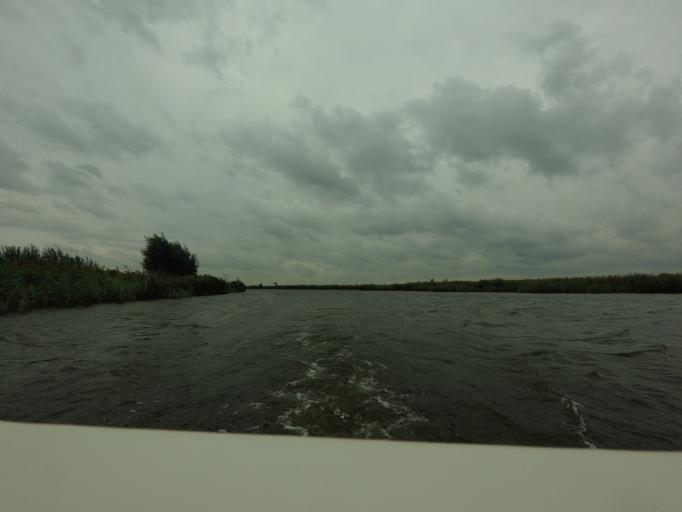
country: NL
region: Friesland
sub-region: Gemeente Boarnsterhim
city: Warten
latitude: 53.1004
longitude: 5.9039
